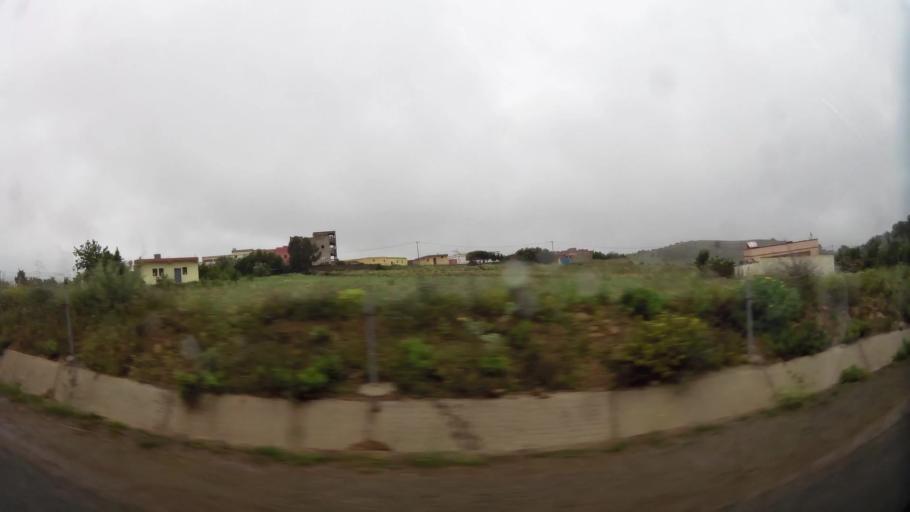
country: MA
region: Oriental
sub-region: Nador
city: Boudinar
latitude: 35.1187
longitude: -3.5759
